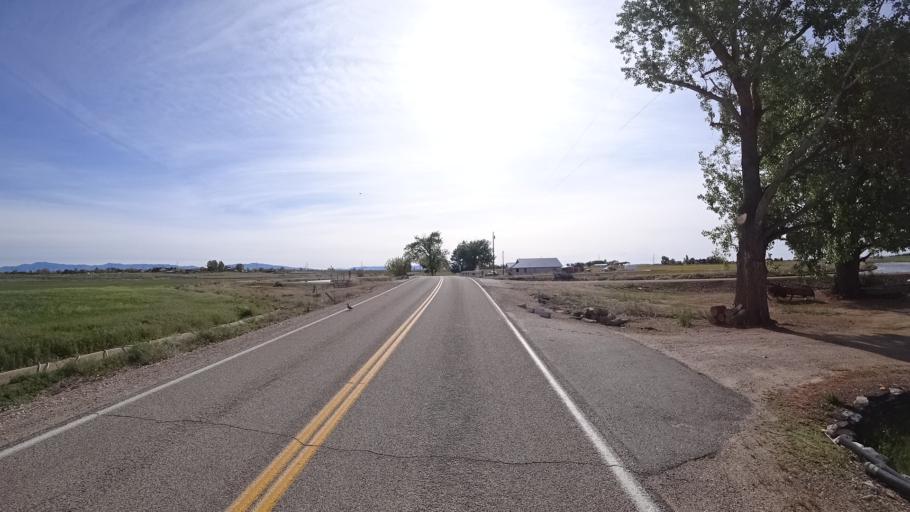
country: US
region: Idaho
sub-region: Ada County
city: Kuna
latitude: 43.4737
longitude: -116.3414
